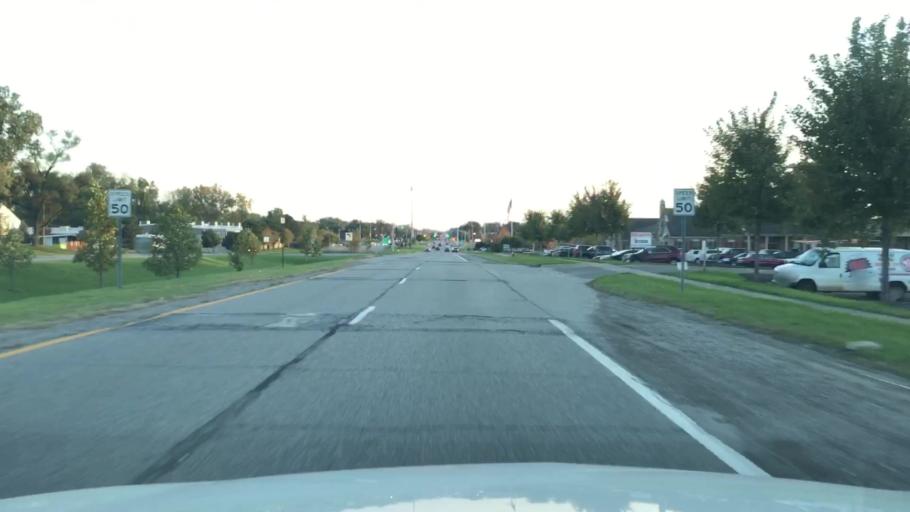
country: US
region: Michigan
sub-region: Macomb County
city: Utica
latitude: 42.6312
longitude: -83.0526
